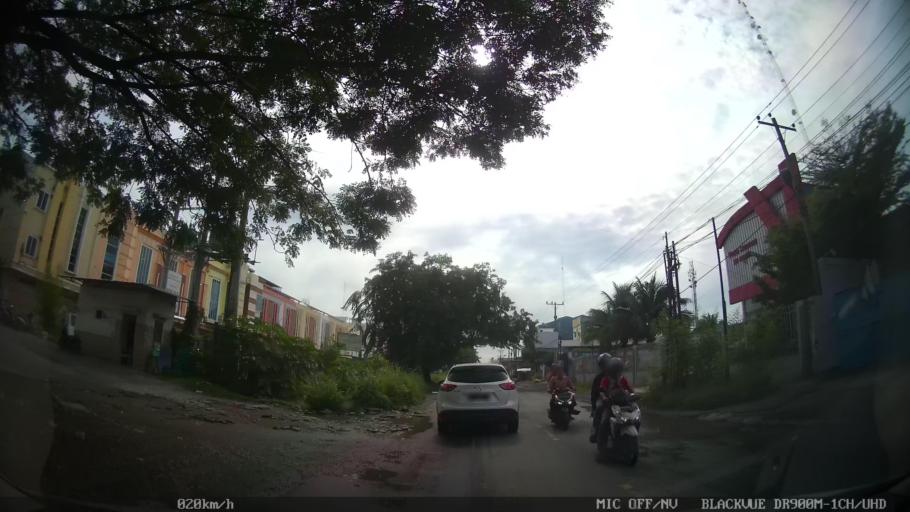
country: ID
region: North Sumatra
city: Medan
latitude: 3.6288
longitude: 98.7014
